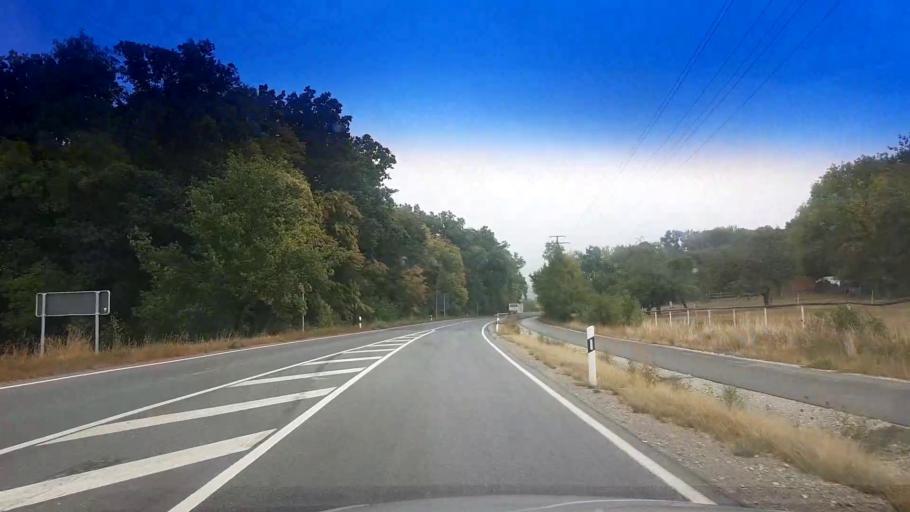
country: DE
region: Bavaria
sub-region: Upper Franconia
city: Buttenheim
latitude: 49.7979
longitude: 11.0289
